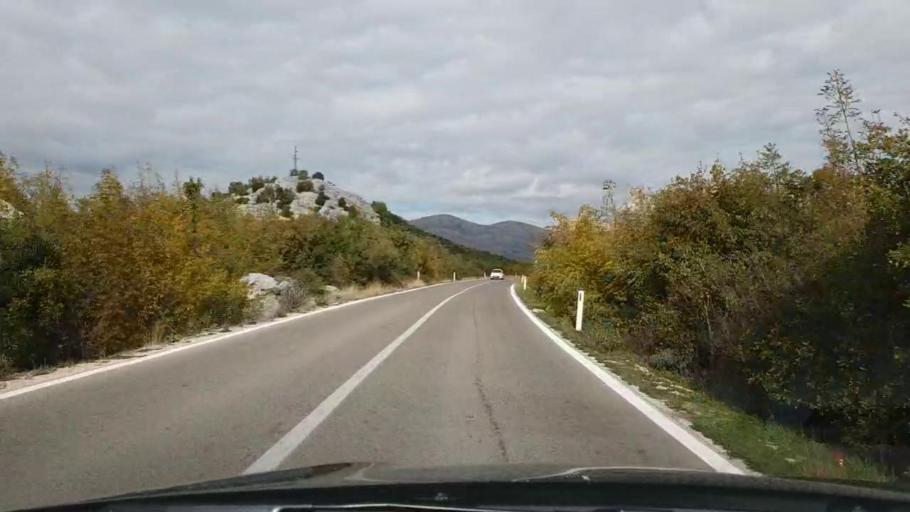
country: HR
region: Dubrovacko-Neretvanska
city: Cibaca
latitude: 42.6824
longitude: 18.2458
